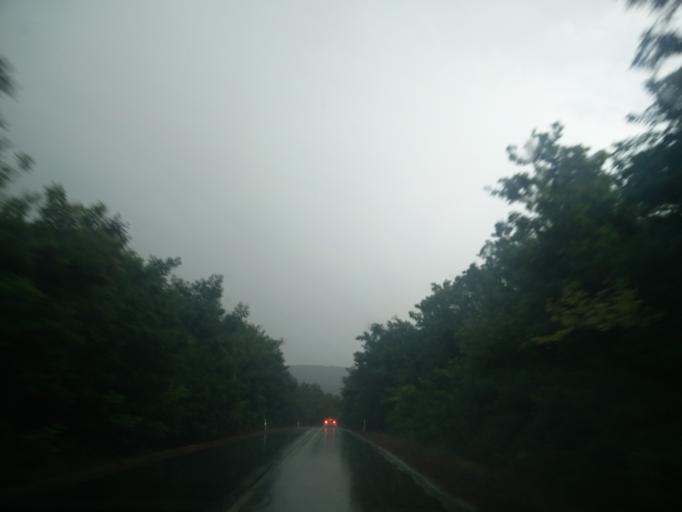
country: HU
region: Pest
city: Biatorbagy
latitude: 47.4579
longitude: 18.7999
